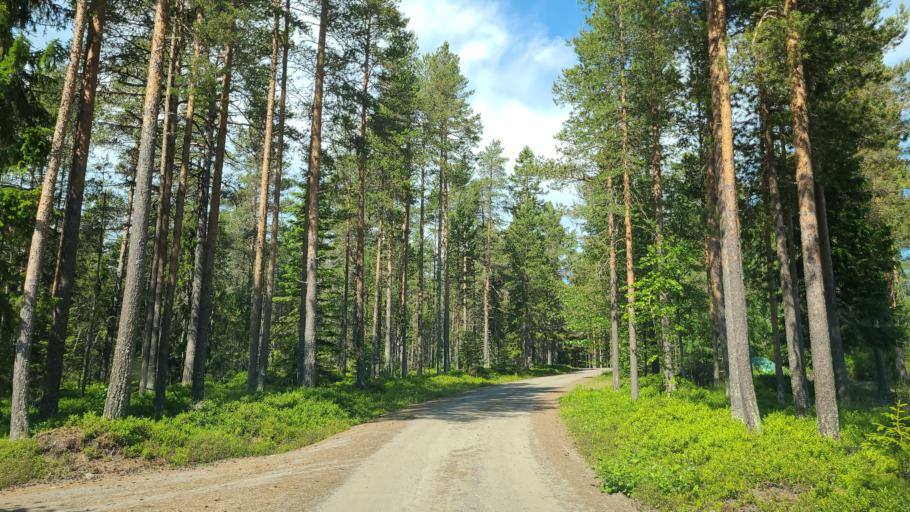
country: SE
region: Vaesterbotten
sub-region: Robertsfors Kommun
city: Robertsfors
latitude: 64.1395
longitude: 20.9625
